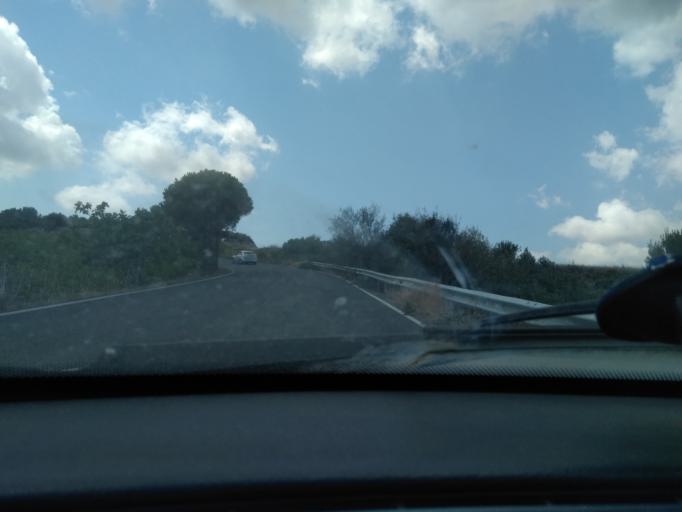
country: GR
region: Crete
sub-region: Nomos Lasithiou
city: Makry-Gialos
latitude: 35.1000
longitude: 26.0597
